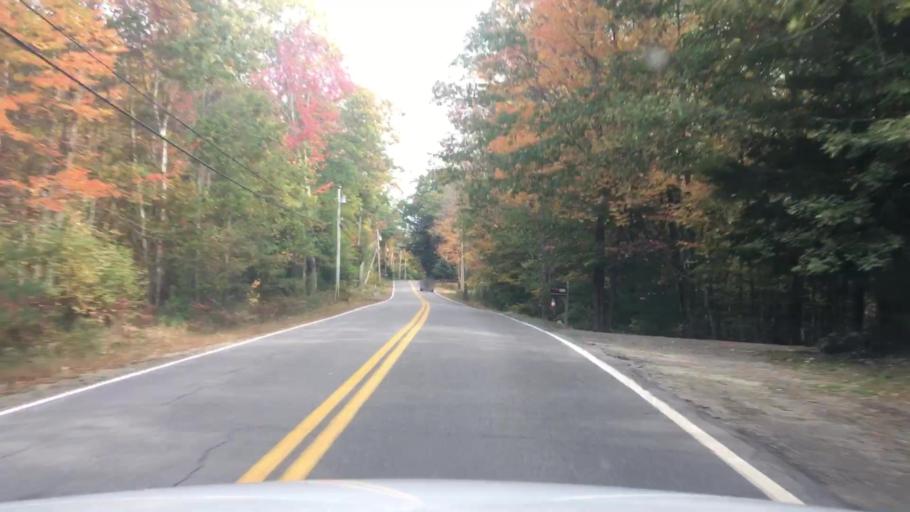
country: US
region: Maine
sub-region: Knox County
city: Hope
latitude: 44.2845
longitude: -69.1226
